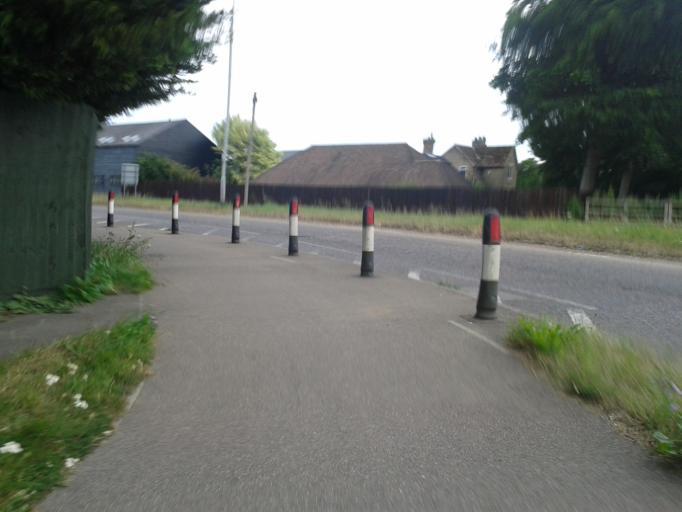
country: GB
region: England
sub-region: Cambridgeshire
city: Sawston
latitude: 52.1657
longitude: 0.1615
